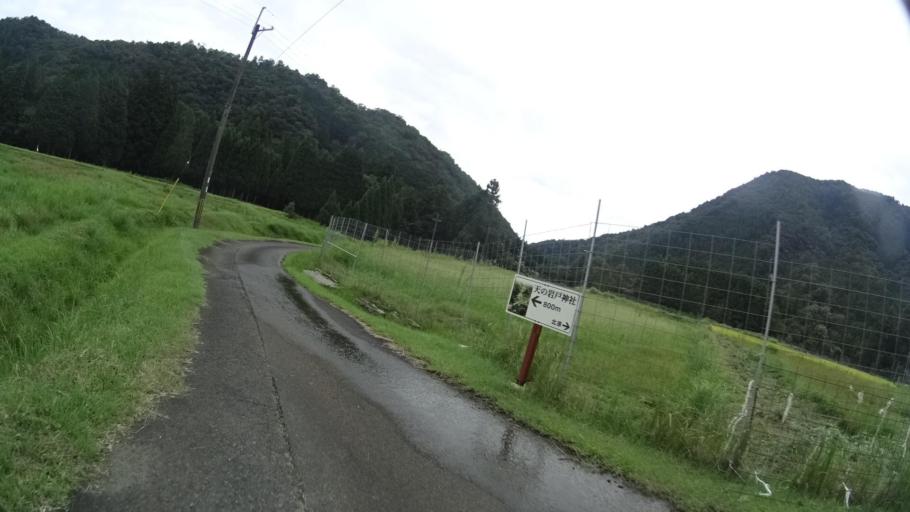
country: JP
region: Kyoto
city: Miyazu
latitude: 35.4368
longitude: 135.1510
